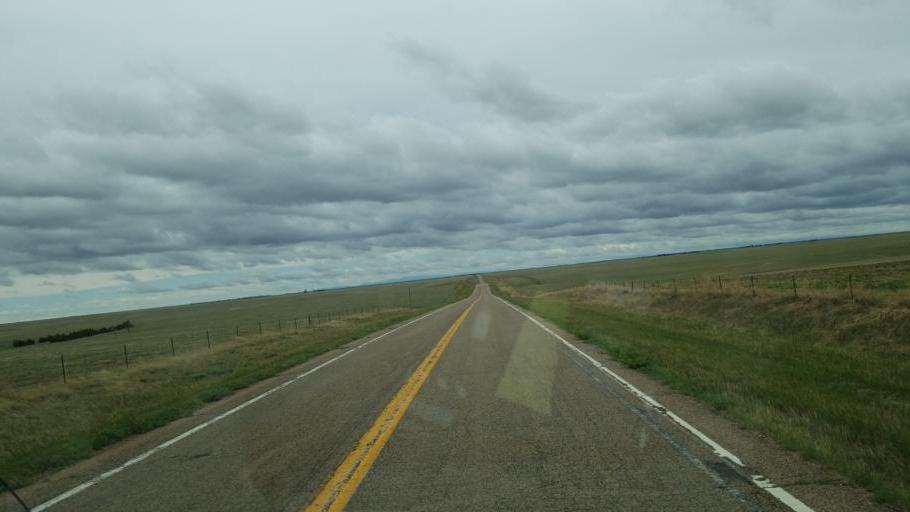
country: US
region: Colorado
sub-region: Lincoln County
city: Limon
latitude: 38.8390
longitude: -103.8934
